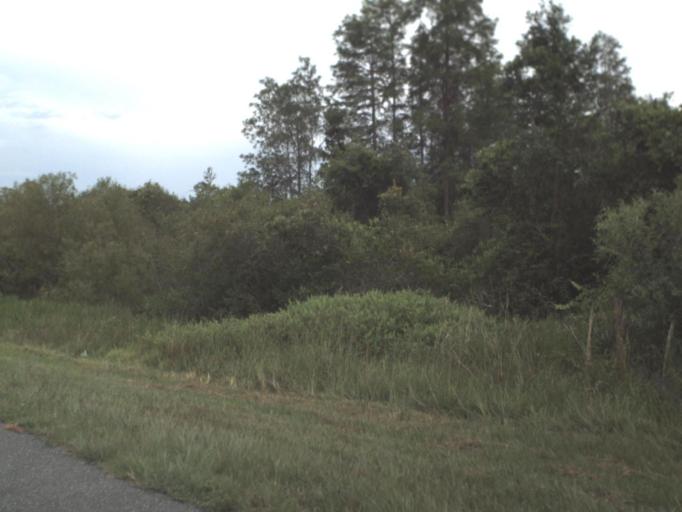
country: US
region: Florida
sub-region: Taylor County
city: Perry
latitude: 30.1253
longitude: -83.3860
